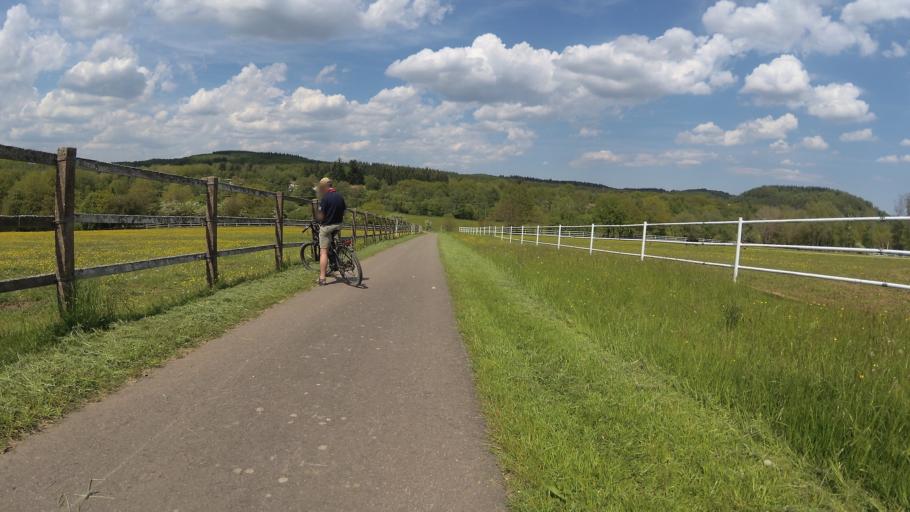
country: DE
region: Rheinland-Pfalz
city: Meckenbach
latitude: 49.5765
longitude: 7.0930
